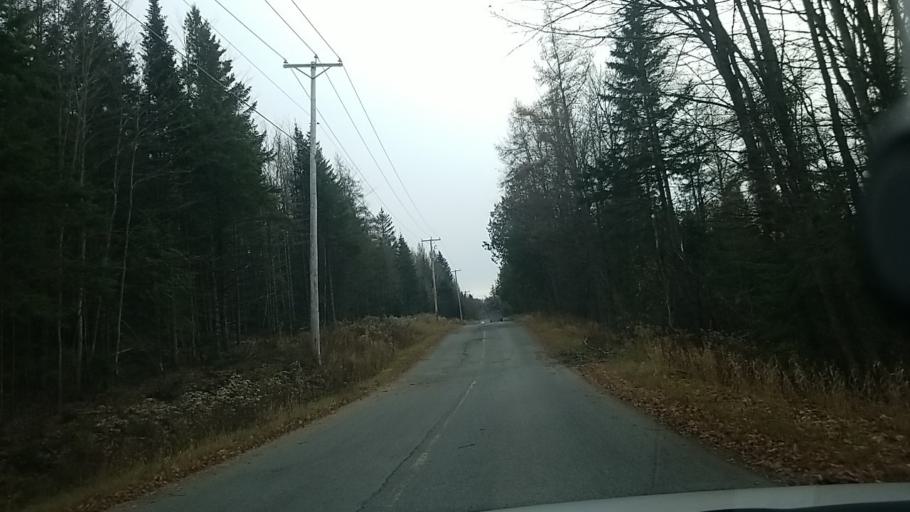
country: CA
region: Quebec
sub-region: Laurentides
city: Saint-Sauveur
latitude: 45.8213
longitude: -74.2484
